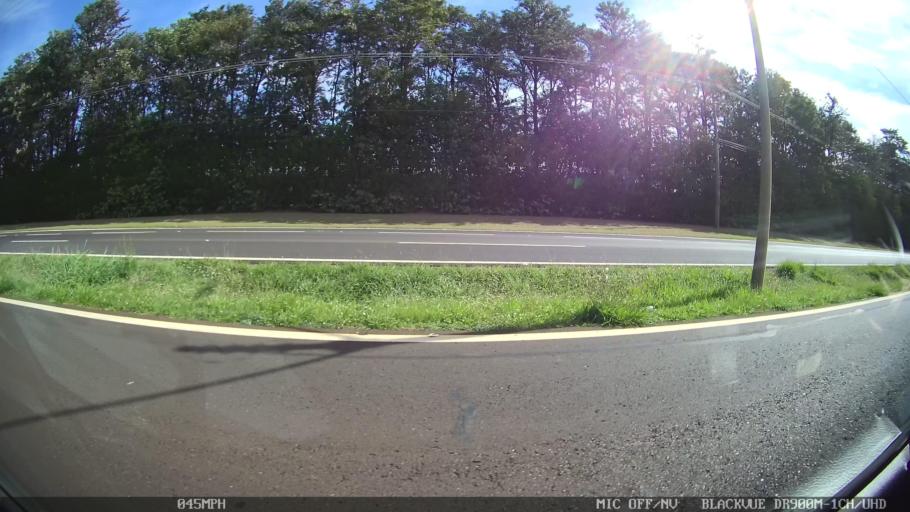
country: BR
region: Sao Paulo
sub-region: Araraquara
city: Araraquara
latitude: -21.8245
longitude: -48.1553
